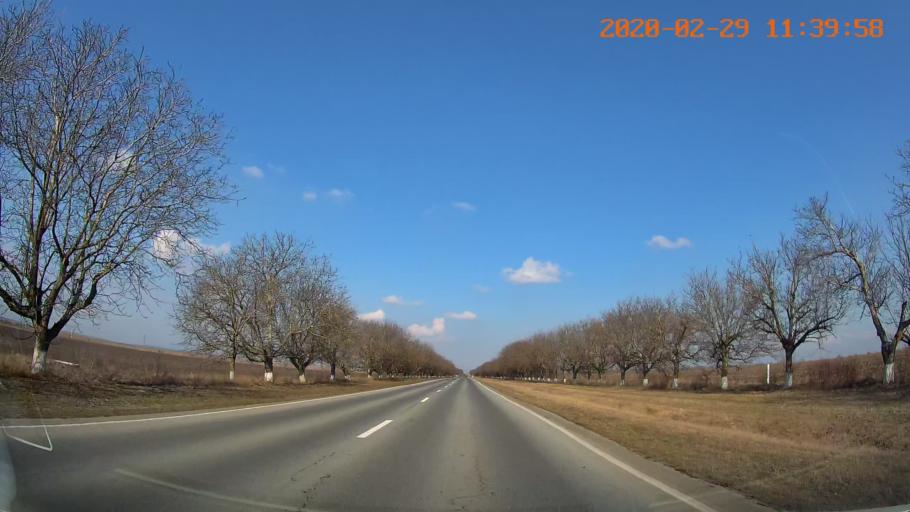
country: MD
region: Rezina
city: Saharna
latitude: 47.6487
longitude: 29.0221
